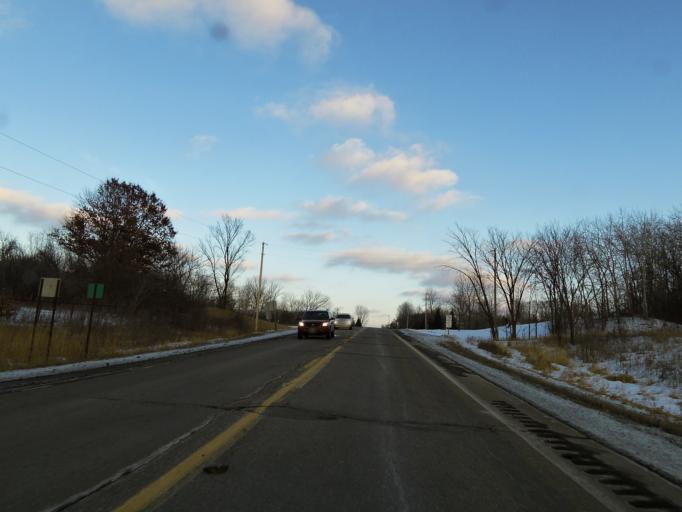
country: US
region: Minnesota
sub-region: Dakota County
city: Lakeville
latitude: 44.6452
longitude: -93.3193
